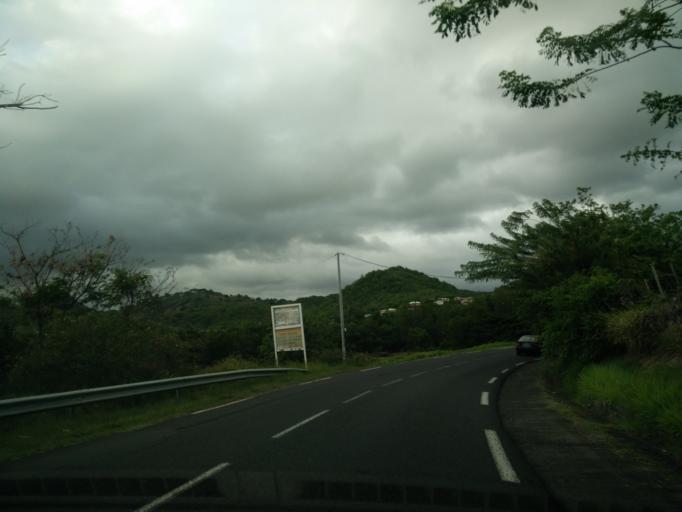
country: MQ
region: Martinique
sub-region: Martinique
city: Le Marin
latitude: 14.4655
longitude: -60.8587
